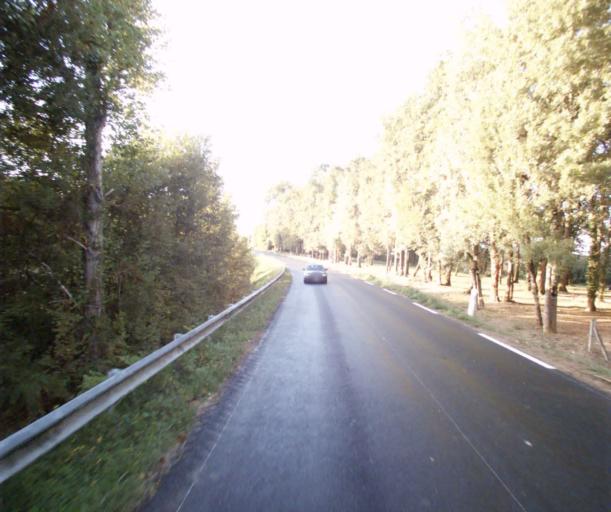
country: FR
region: Midi-Pyrenees
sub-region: Departement du Gers
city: Cazaubon
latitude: 43.9191
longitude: -0.0299
